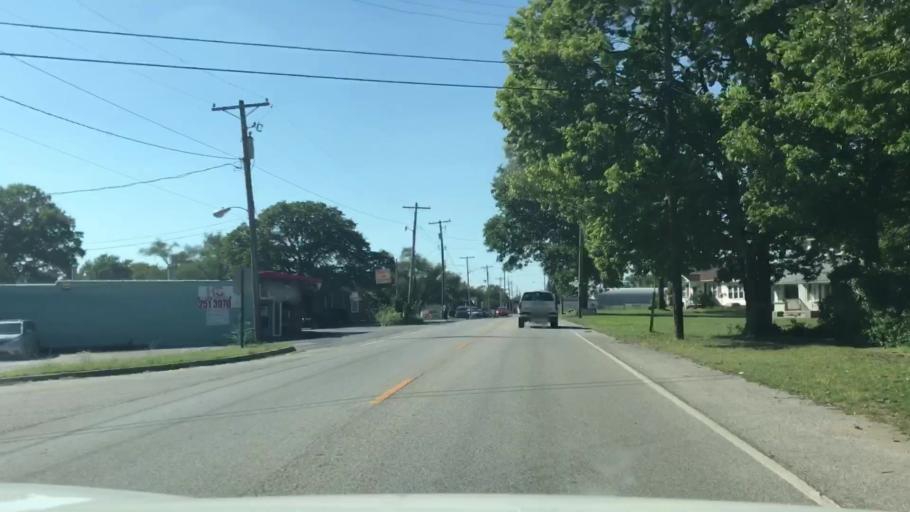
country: US
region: Illinois
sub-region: Madison County
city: Wood River
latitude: 38.8664
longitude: -90.0841
